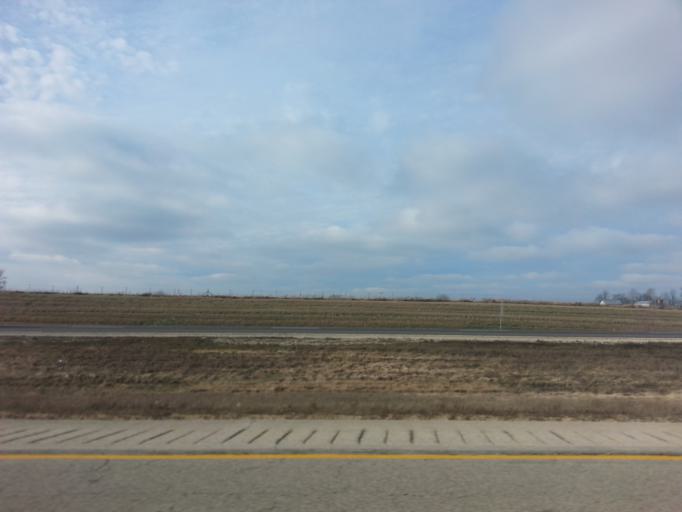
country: US
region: Illinois
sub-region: Ogle County
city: Davis Junction
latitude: 42.1339
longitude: -89.0230
